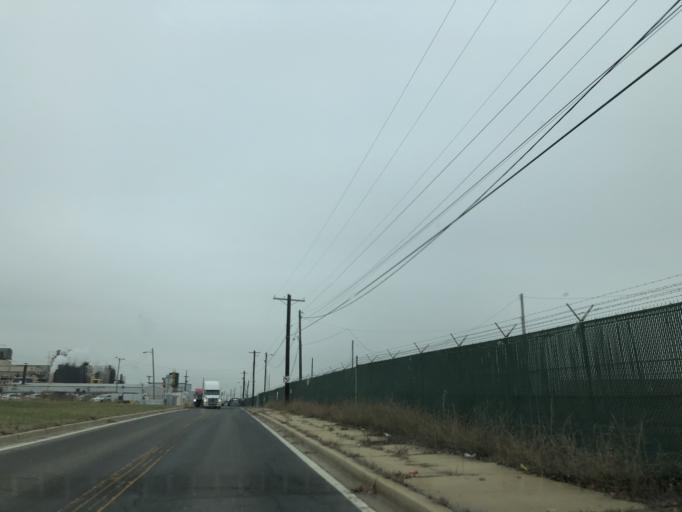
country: US
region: Delaware
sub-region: New Castle County
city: Edgemoor
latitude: 39.7512
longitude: -75.5002
